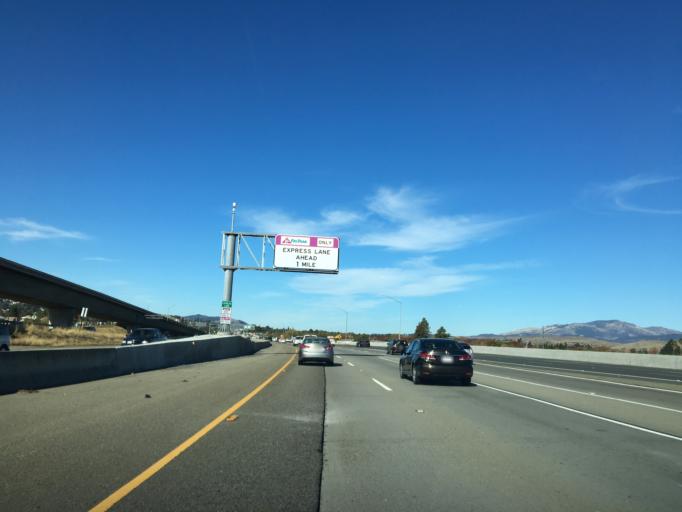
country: US
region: California
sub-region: Alameda County
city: Dublin
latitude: 37.7031
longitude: -121.9235
